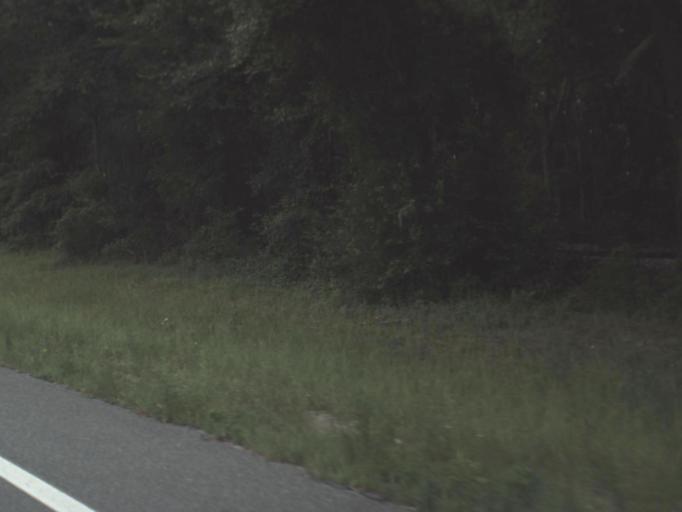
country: US
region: Florida
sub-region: Suwannee County
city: Wellborn
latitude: 30.3169
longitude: -82.7211
